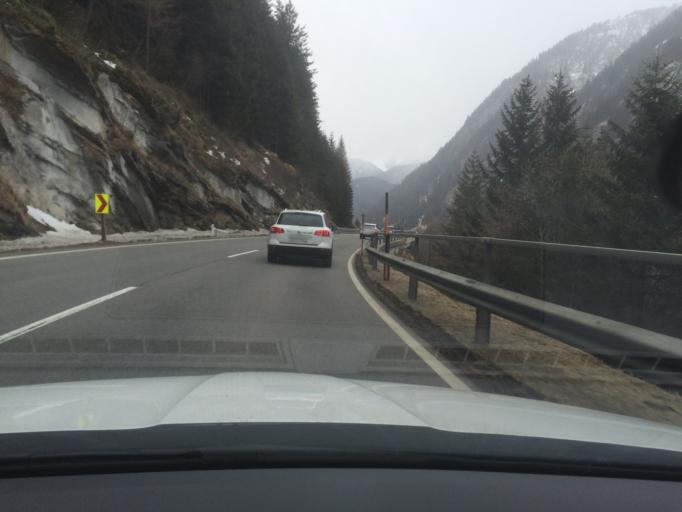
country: AT
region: Tyrol
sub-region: Politischer Bezirk Lienz
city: Matrei in Osttirol
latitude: 47.0877
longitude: 12.5308
